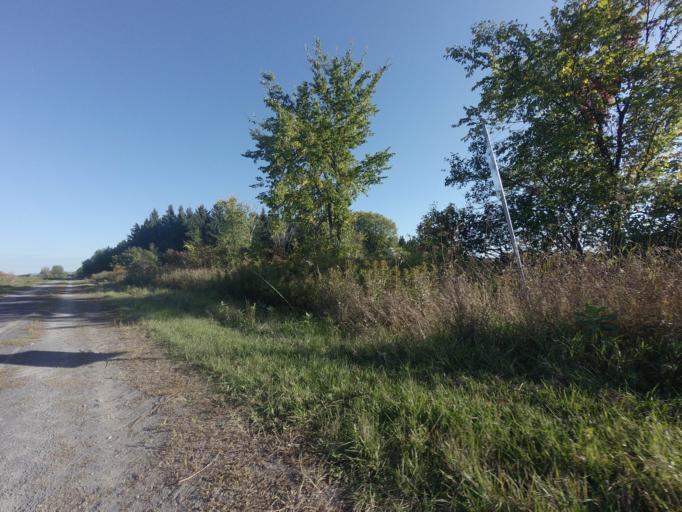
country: CA
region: Ontario
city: Hawkesbury
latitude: 45.5191
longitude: -74.5275
